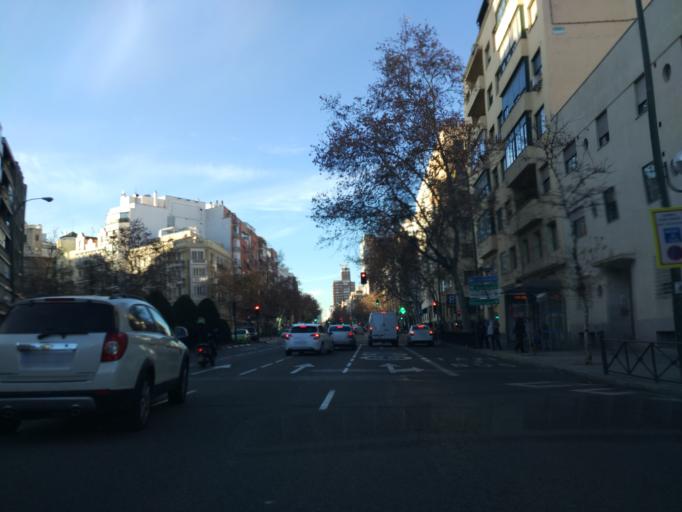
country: ES
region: Madrid
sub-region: Provincia de Madrid
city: Salamanca
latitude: 40.4318
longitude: -3.6718
